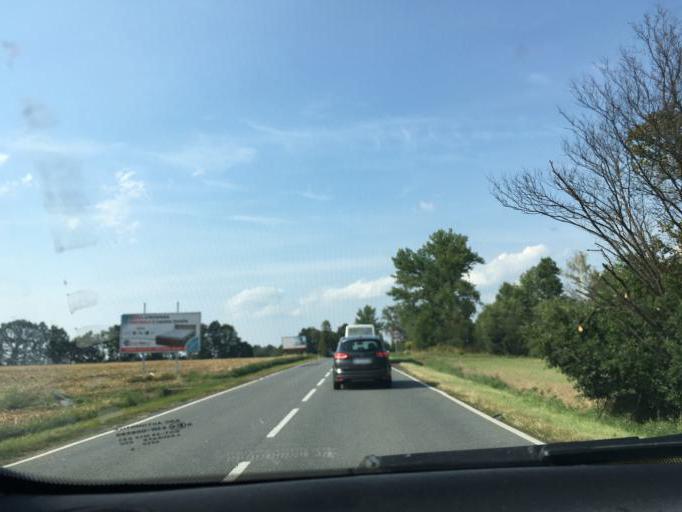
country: PL
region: Opole Voivodeship
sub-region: Powiat prudnicki
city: Laka Prudnicka
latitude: 50.3680
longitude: 17.5379
